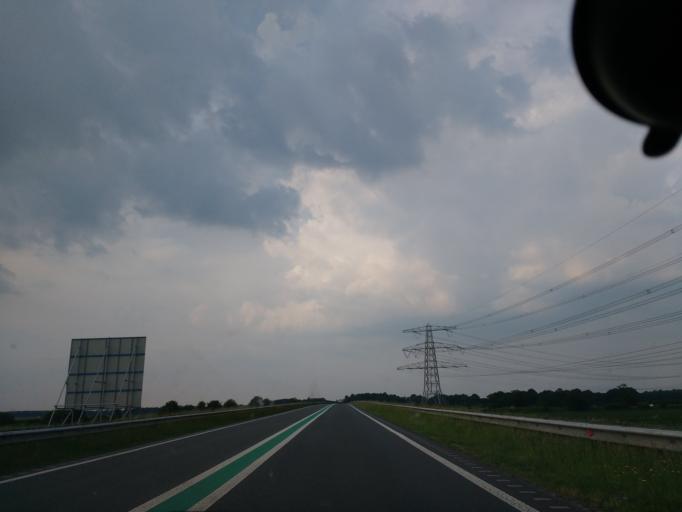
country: NL
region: Drenthe
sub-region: Gemeente Coevorden
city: Sleen
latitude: 52.8004
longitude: 6.8528
